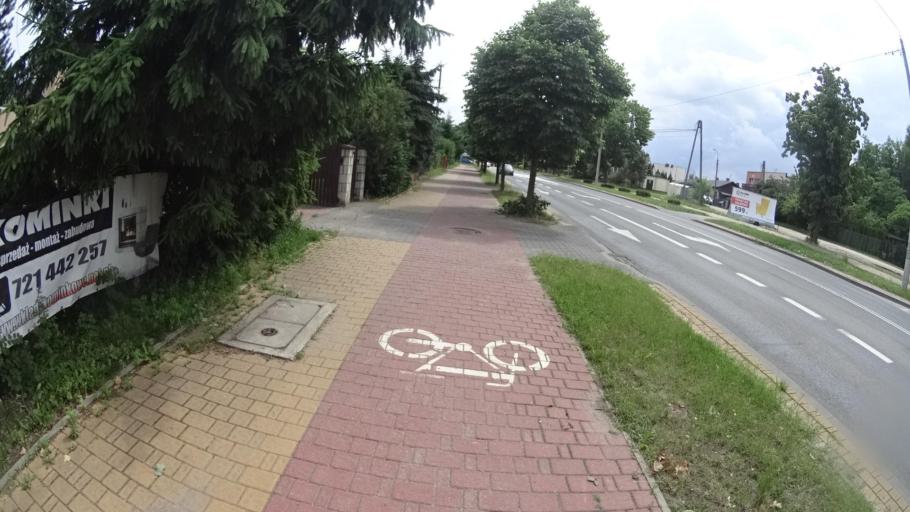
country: PL
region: Masovian Voivodeship
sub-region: Powiat grojecki
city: Grojec
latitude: 51.8574
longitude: 20.8696
